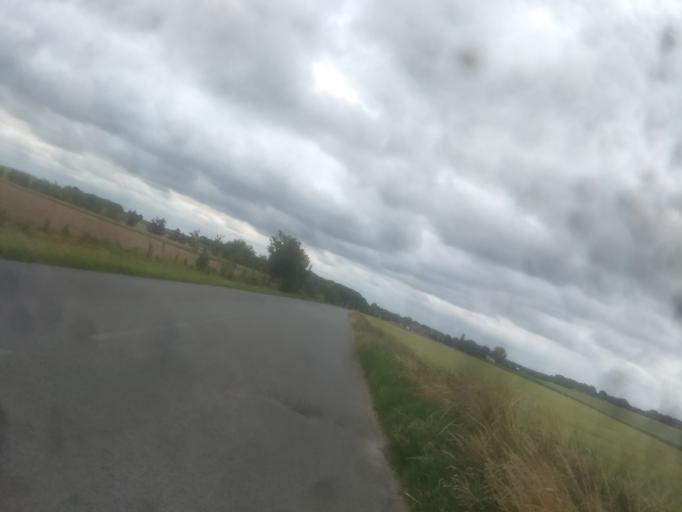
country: FR
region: Nord-Pas-de-Calais
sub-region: Departement du Pas-de-Calais
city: Thelus
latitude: 50.3353
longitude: 2.7943
